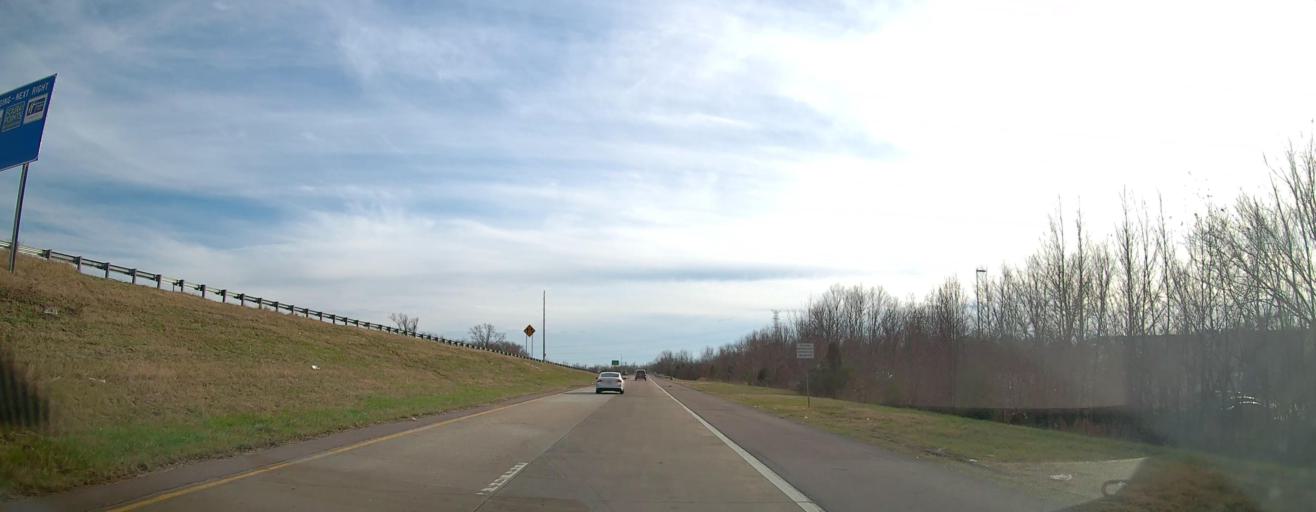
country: US
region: Tennessee
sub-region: Shelby County
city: Germantown
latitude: 35.0486
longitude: -89.8096
